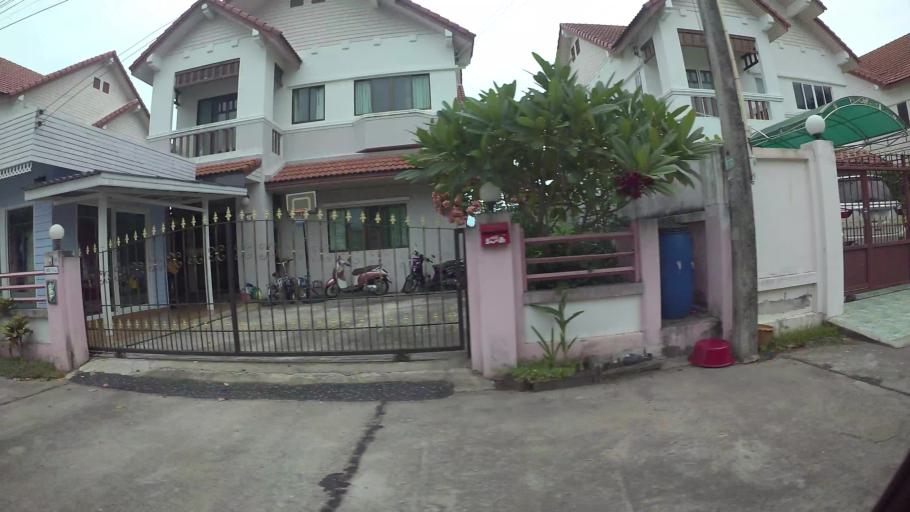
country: TH
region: Chon Buri
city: Si Racha
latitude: 13.1489
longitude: 100.9848
